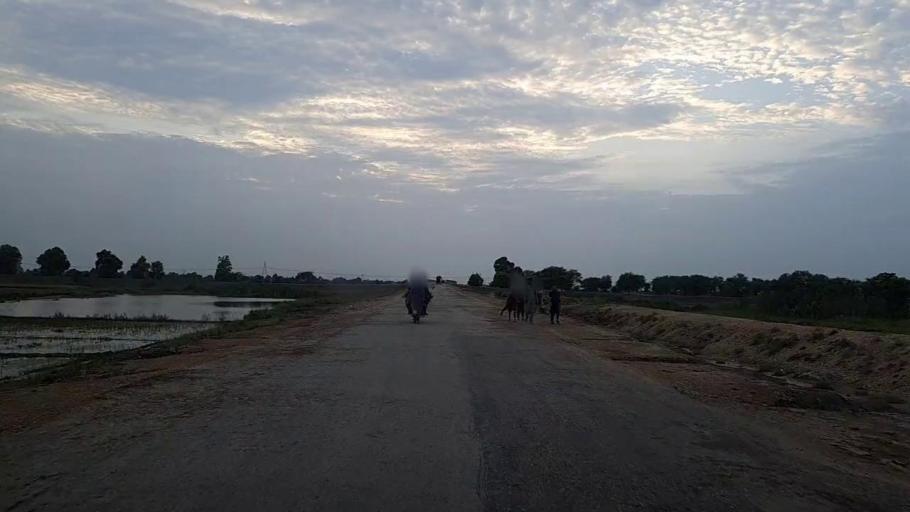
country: PK
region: Sindh
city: Naushahro Firoz
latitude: 26.8228
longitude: 68.1621
